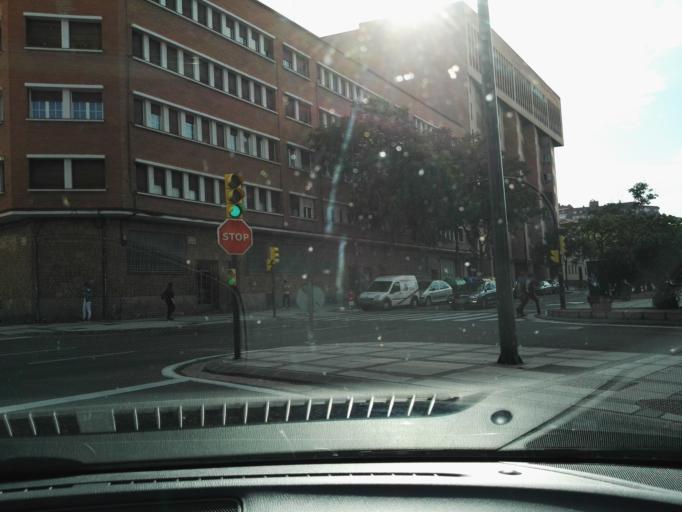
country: ES
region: Aragon
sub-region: Provincia de Zaragoza
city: Zaragoza
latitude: 41.6390
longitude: -0.8710
